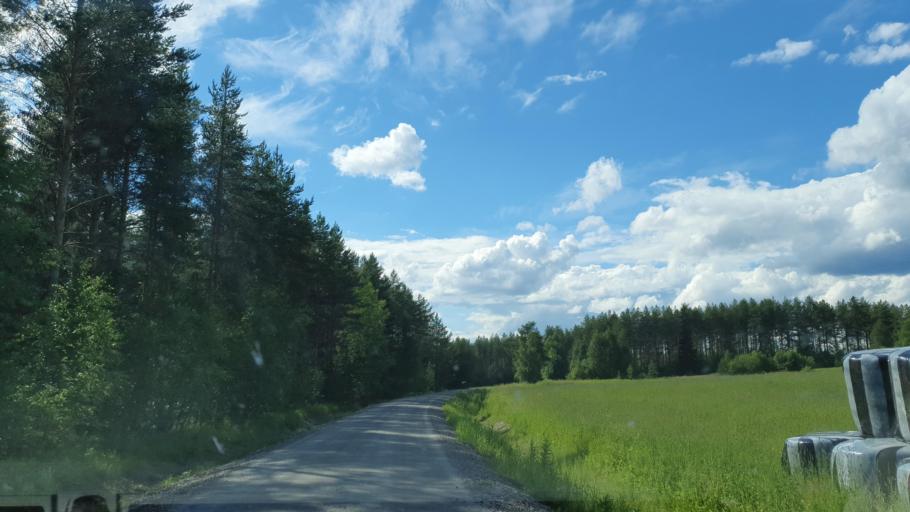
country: FI
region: Kainuu
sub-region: Kehys-Kainuu
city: Kuhmo
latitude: 64.1468
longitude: 29.7575
